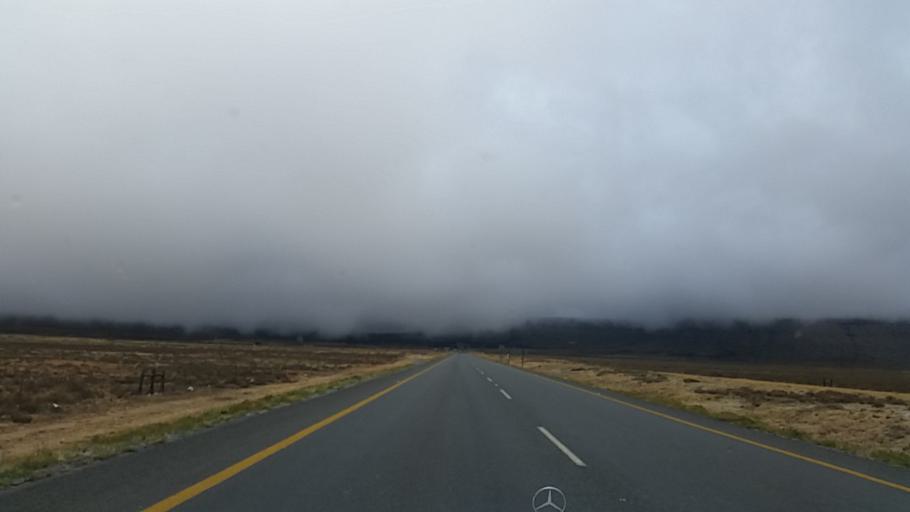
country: ZA
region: Eastern Cape
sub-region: Cacadu District Municipality
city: Graaff-Reinet
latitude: -31.9279
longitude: 24.7470
